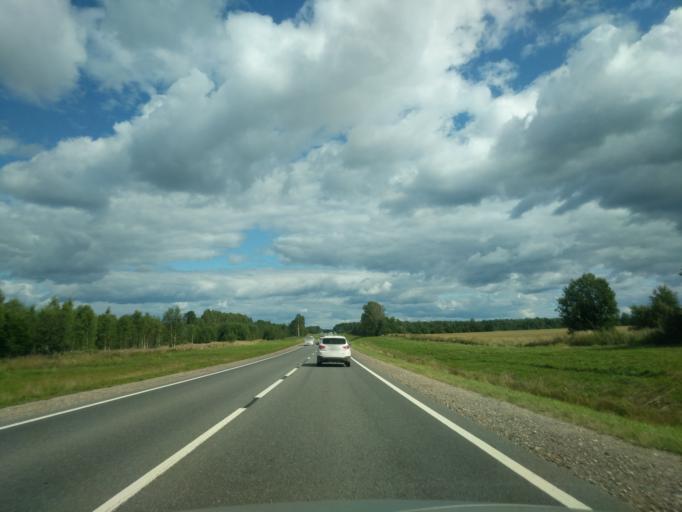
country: RU
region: Kostroma
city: Oktyabr'skiy
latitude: 57.7979
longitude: 41.2103
